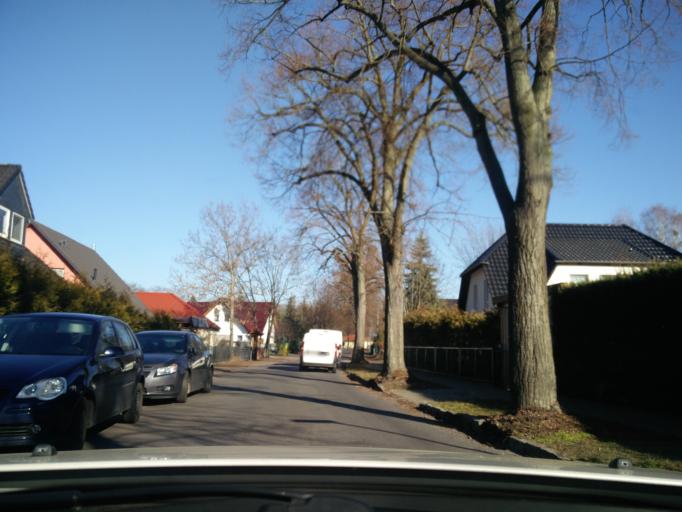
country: DE
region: Brandenburg
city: Brieselang
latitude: 52.5777
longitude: 12.9965
